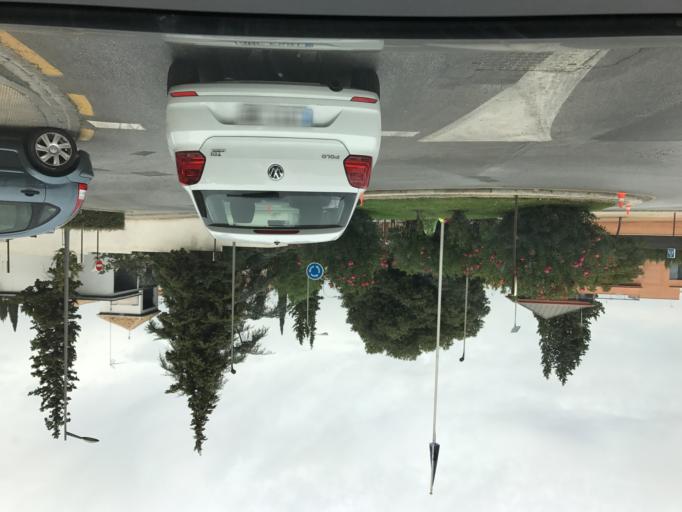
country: ES
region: Andalusia
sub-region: Provincia de Granada
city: Huetor Vega
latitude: 37.1600
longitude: -3.5893
